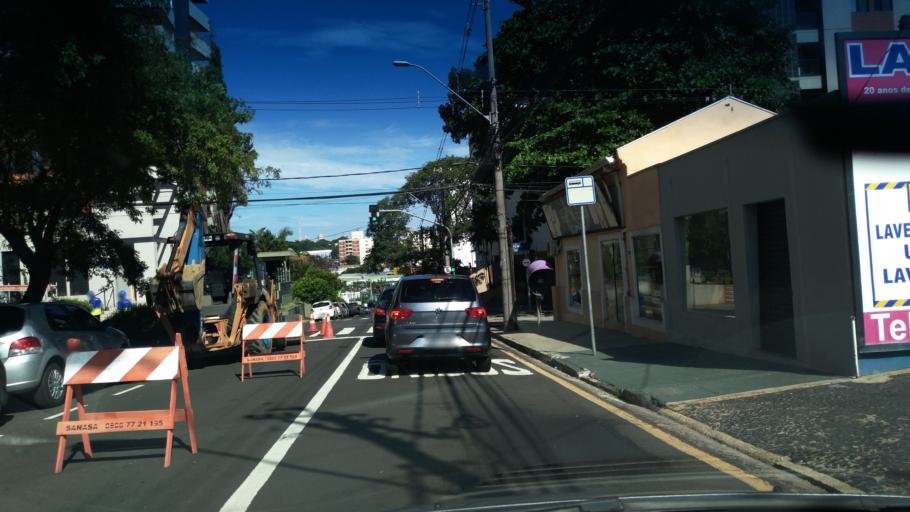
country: BR
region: Sao Paulo
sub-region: Campinas
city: Campinas
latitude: -22.8900
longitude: -47.0554
